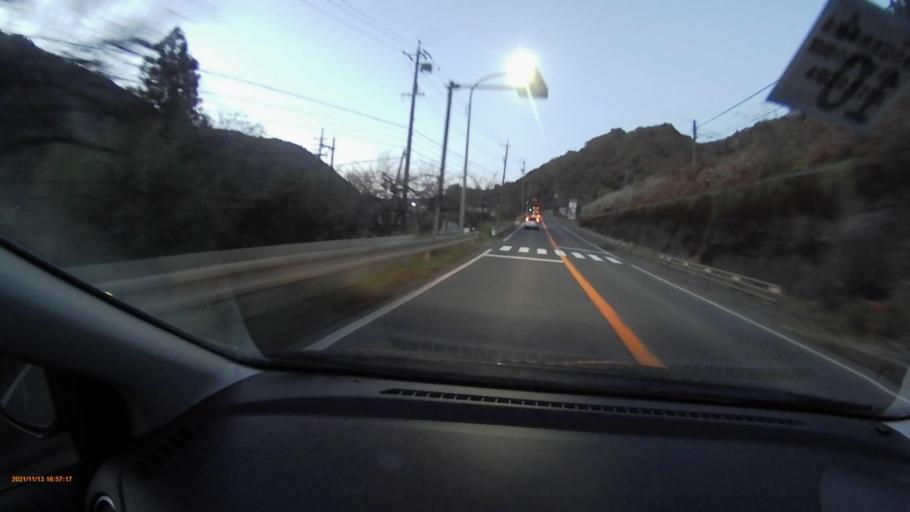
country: JP
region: Nagano
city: Iida
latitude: 35.7379
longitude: 137.7164
